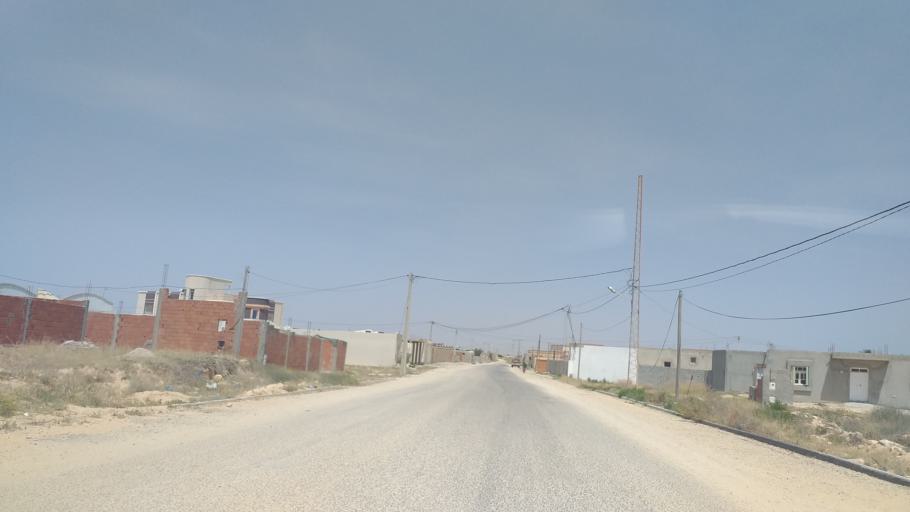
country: TN
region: Qabis
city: Gabes
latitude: 33.9551
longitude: 10.0655
